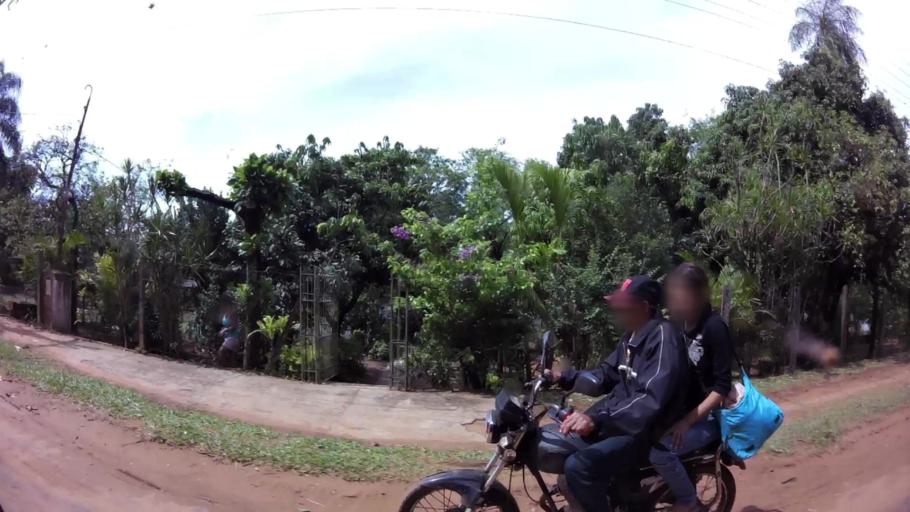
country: PY
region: Central
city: Limpio
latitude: -25.1856
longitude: -57.4554
